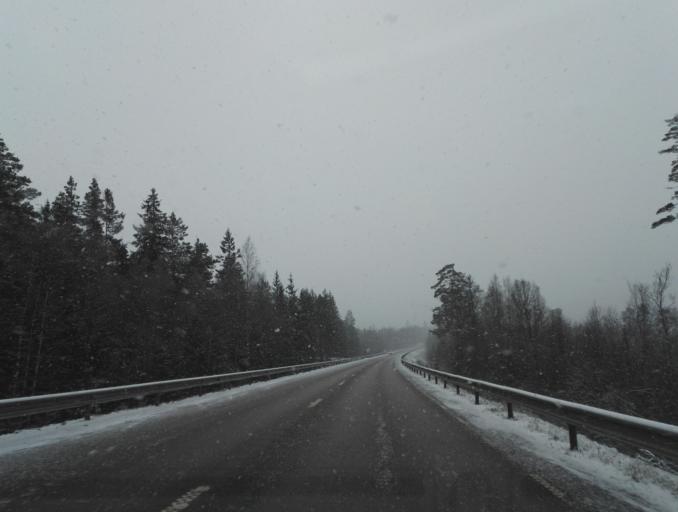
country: SE
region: Kronoberg
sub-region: Uppvidinge Kommun
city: Lenhovda
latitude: 57.0971
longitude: 15.2013
